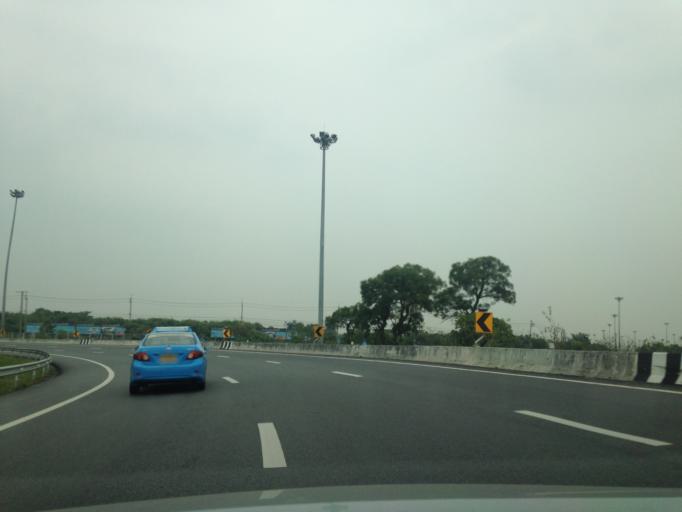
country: TH
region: Bangkok
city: Saphan Sung
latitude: 13.7802
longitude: 100.6869
